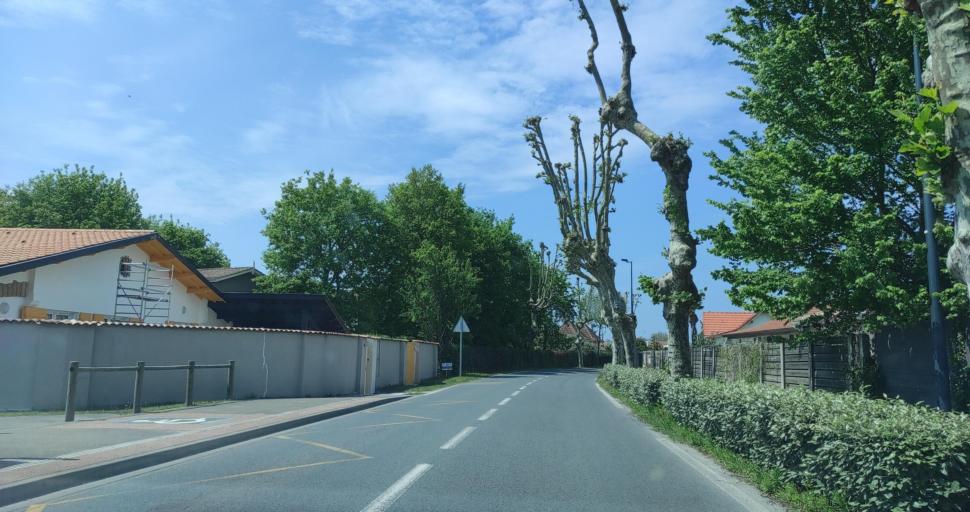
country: FR
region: Aquitaine
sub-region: Departement de la Gironde
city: Ares
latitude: 44.7629
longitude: -1.1326
